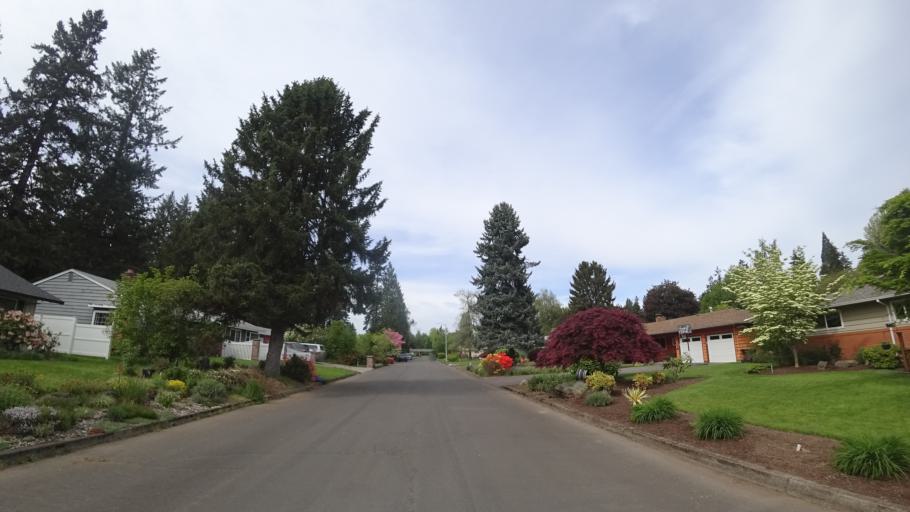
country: US
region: Oregon
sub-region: Washington County
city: Hillsboro
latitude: 45.5097
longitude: -122.9457
